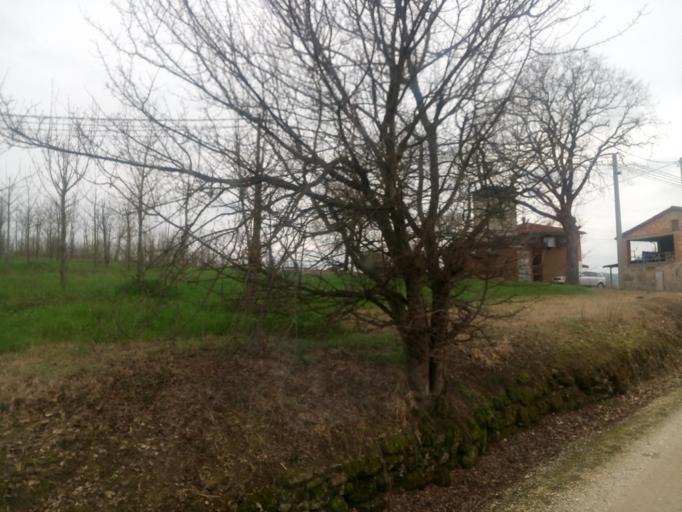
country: IT
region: Emilia-Romagna
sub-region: Forli-Cesena
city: Meldola
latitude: 44.1212
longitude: 12.0804
